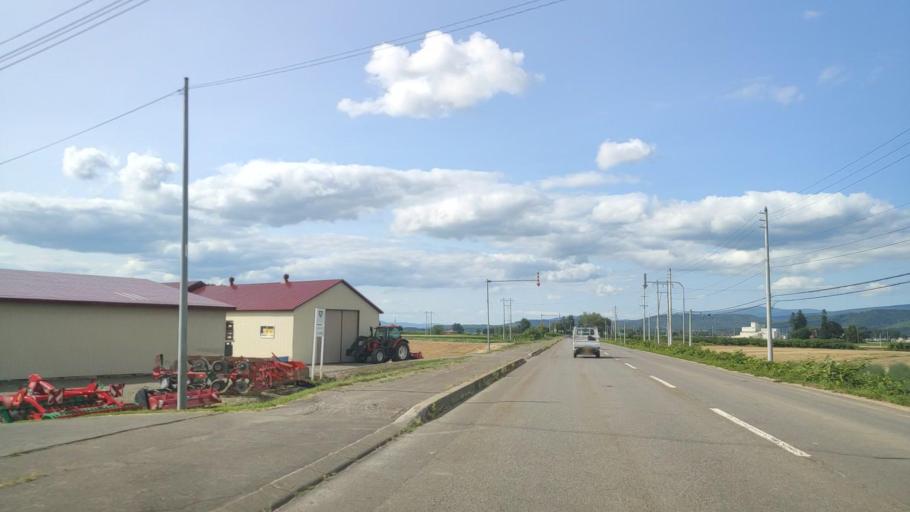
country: JP
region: Hokkaido
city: Nayoro
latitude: 44.4245
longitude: 142.4006
